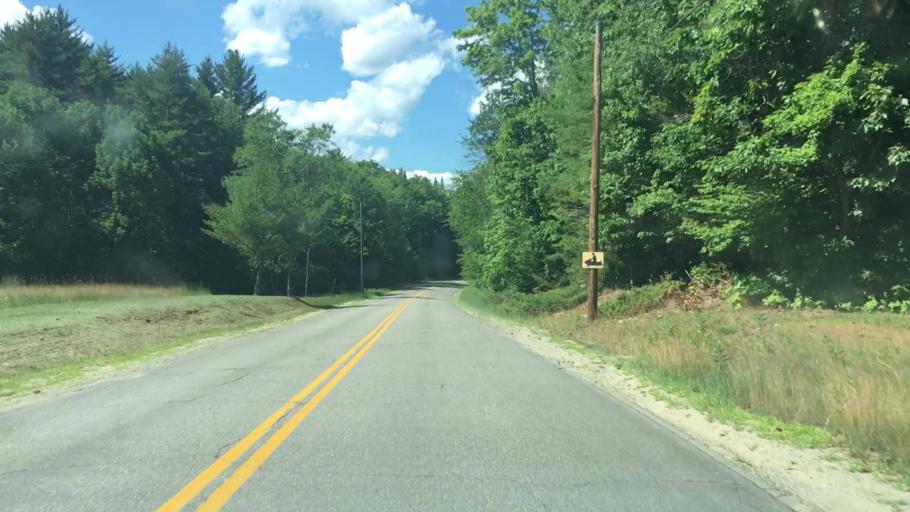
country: US
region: Maine
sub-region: Franklin County
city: Chesterville
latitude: 44.5708
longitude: -70.0885
